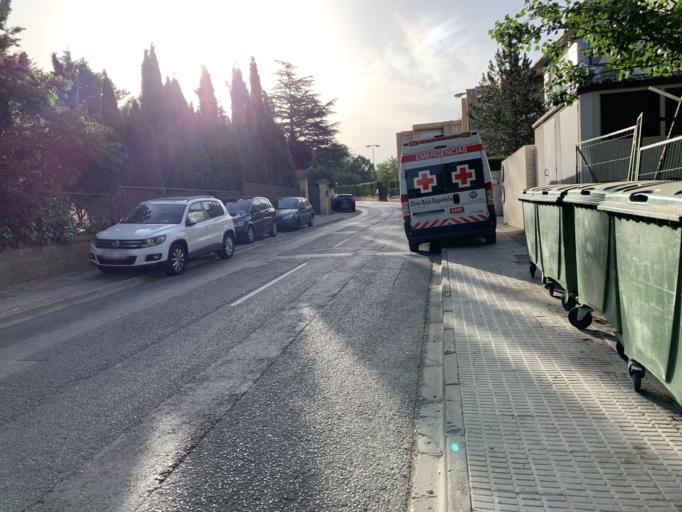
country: ES
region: Aragon
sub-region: Provincia de Teruel
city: Teruel
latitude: 40.3536
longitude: -1.1103
